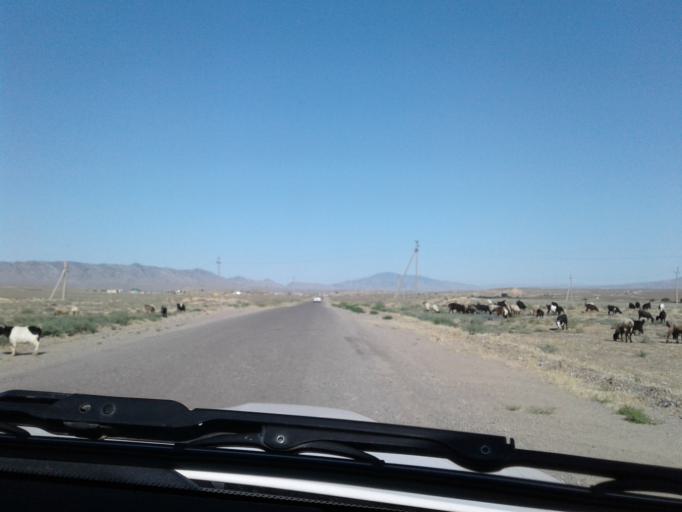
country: TM
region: Balkan
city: Magtymguly
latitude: 38.6859
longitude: 56.4391
